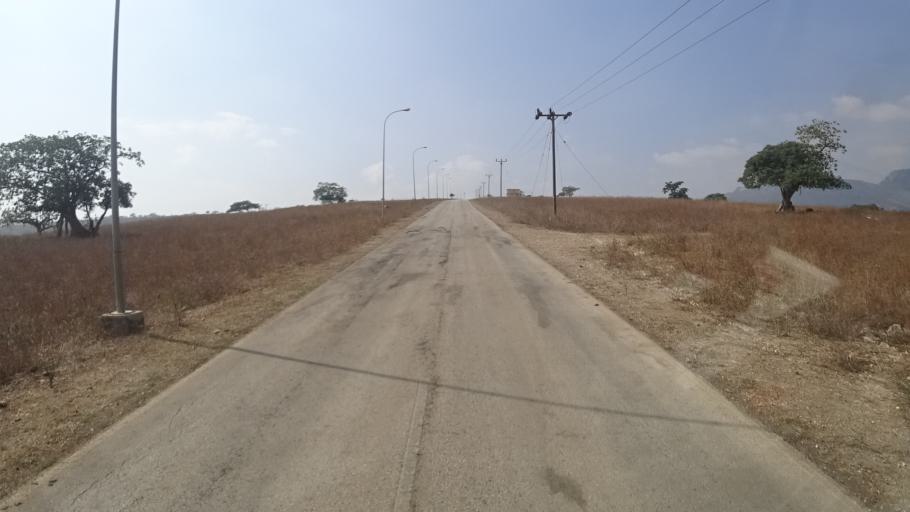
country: YE
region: Al Mahrah
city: Hawf
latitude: 16.7300
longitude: 53.2708
